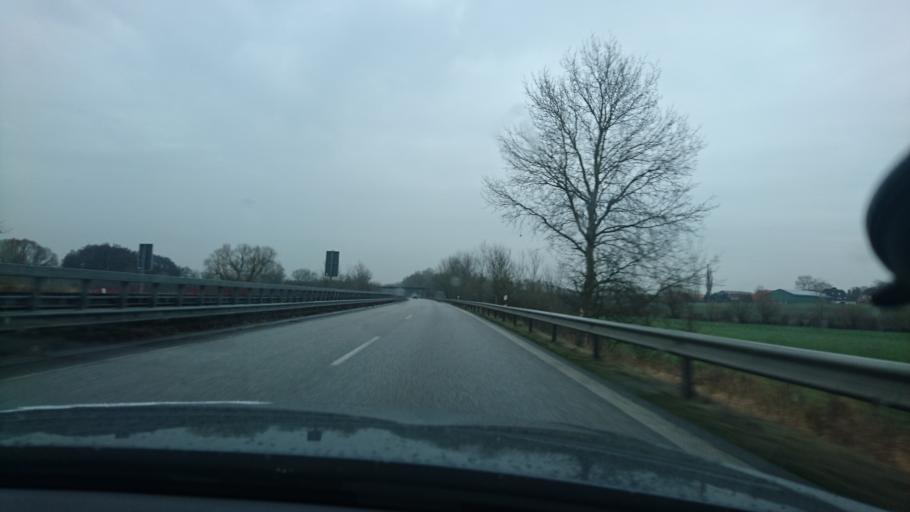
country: DE
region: Schleswig-Holstein
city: Altenkrempe
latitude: 54.1339
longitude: 10.8372
